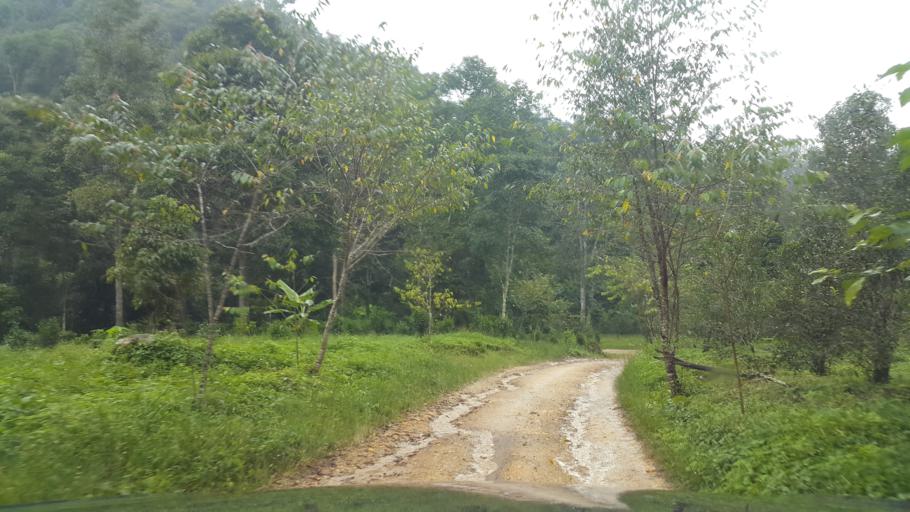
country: TH
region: Chiang Rai
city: Wiang Pa Pao
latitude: 19.1322
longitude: 99.3569
